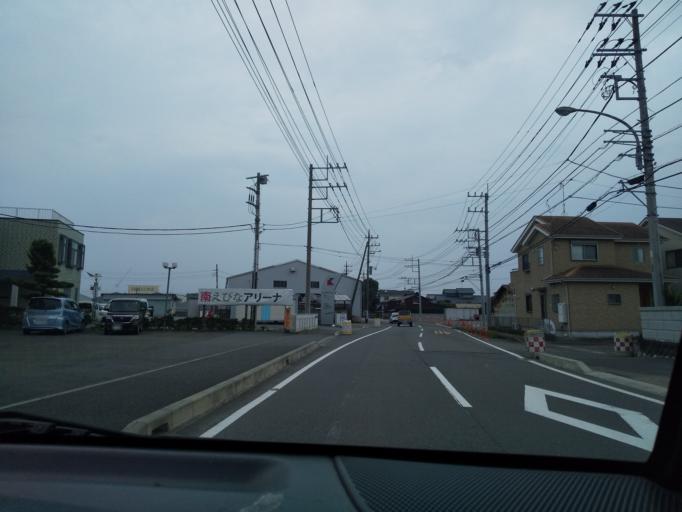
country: JP
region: Kanagawa
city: Atsugi
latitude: 35.4094
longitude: 139.3897
